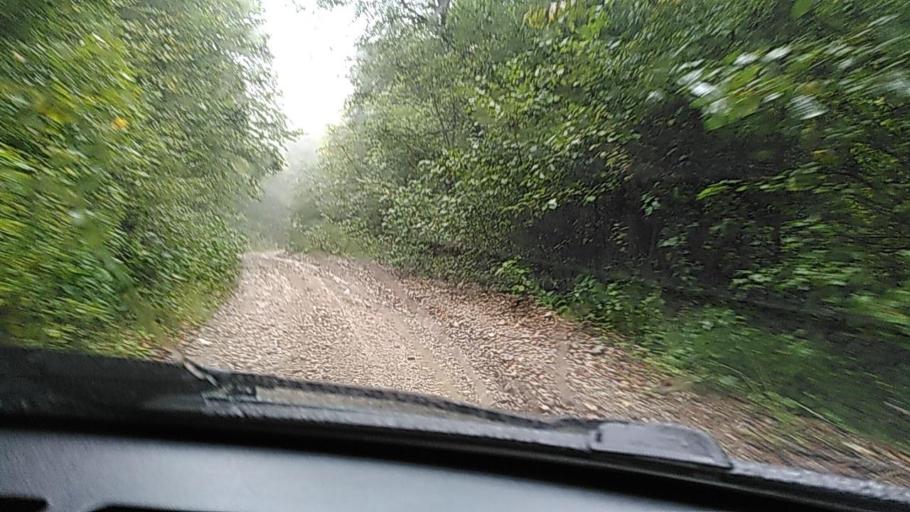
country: RU
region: Kabardino-Balkariya
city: Belaya Rechka
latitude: 43.3740
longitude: 43.4288
